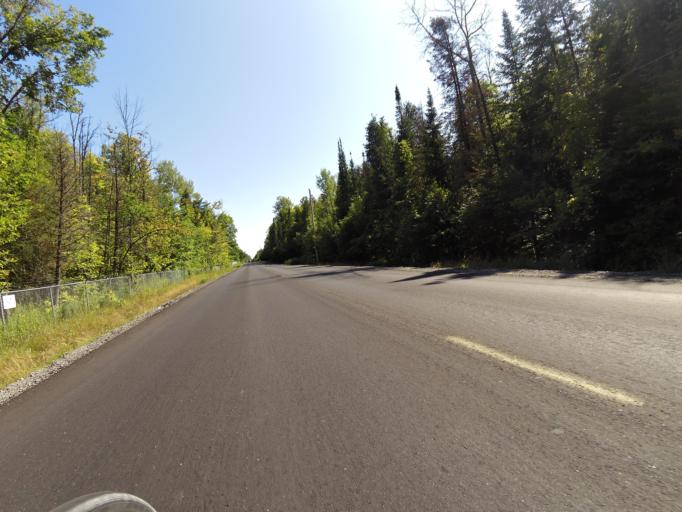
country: CA
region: Ontario
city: Bells Corners
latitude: 45.3835
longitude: -75.9453
